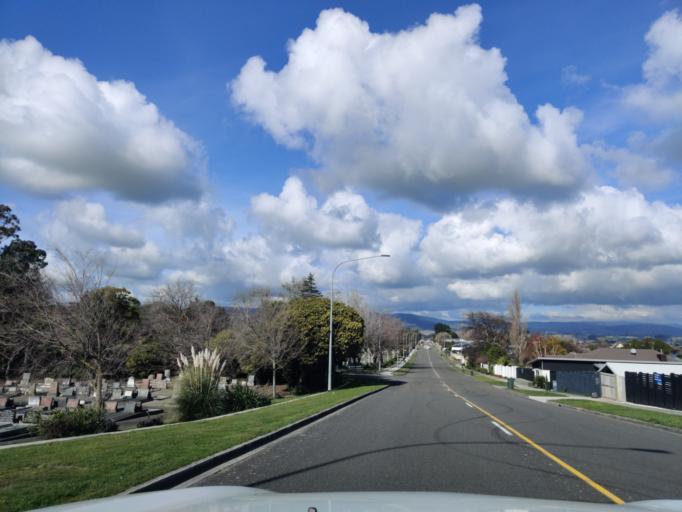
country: NZ
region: Manawatu-Wanganui
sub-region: Palmerston North City
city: Palmerston North
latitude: -40.3234
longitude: 175.6604
